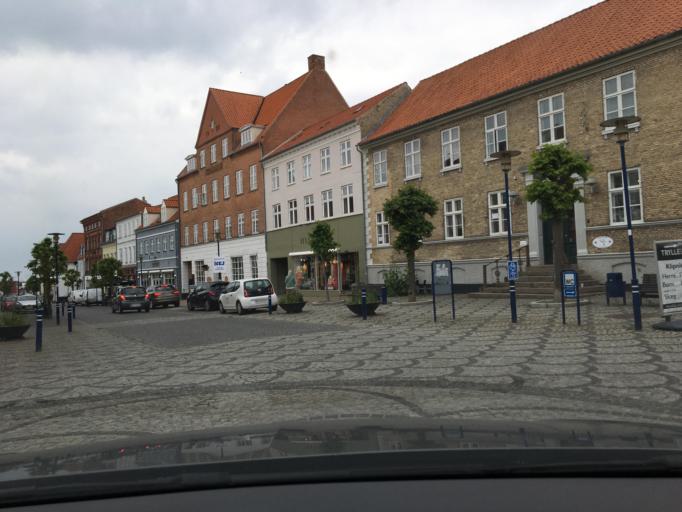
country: DK
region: South Denmark
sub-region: Assens Kommune
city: Assens
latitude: 55.2700
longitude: 9.8964
